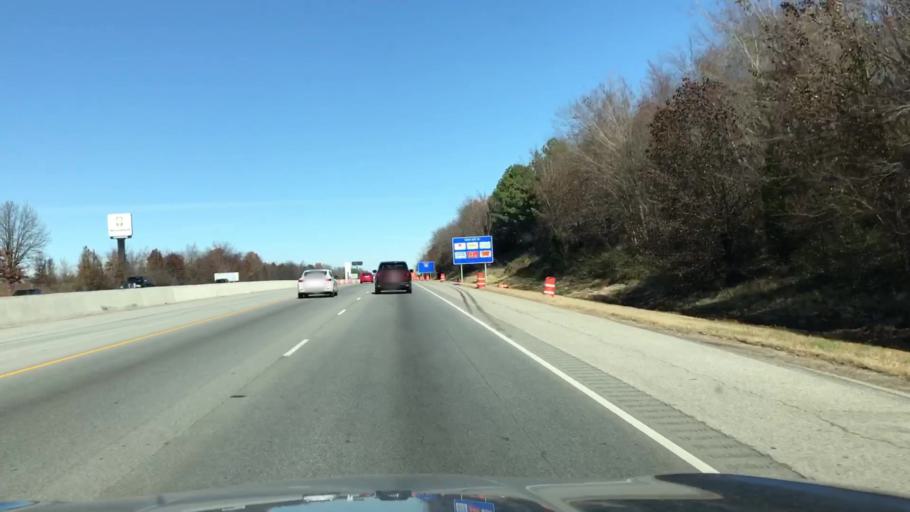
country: US
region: Arkansas
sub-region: Benton County
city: Bentonville
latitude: 36.3250
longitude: -94.1846
